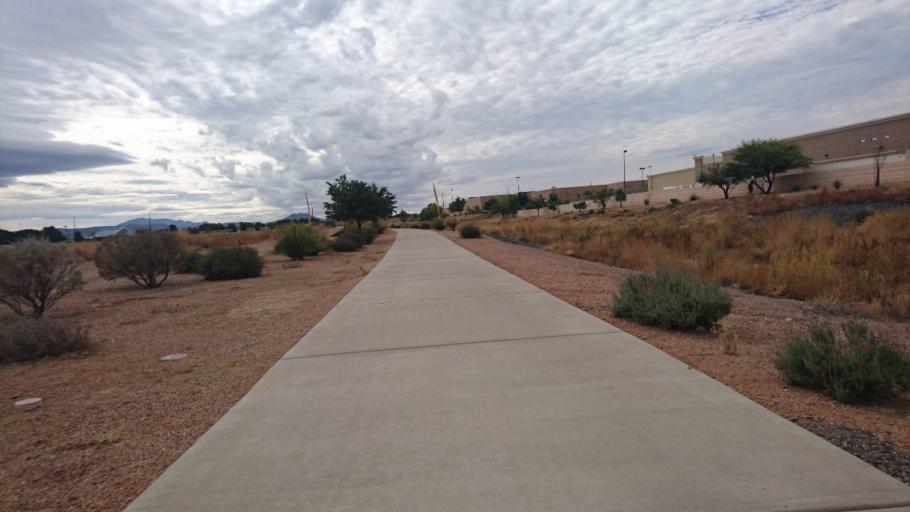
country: US
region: Arizona
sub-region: Mohave County
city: Kingman
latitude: 35.2231
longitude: -114.0313
